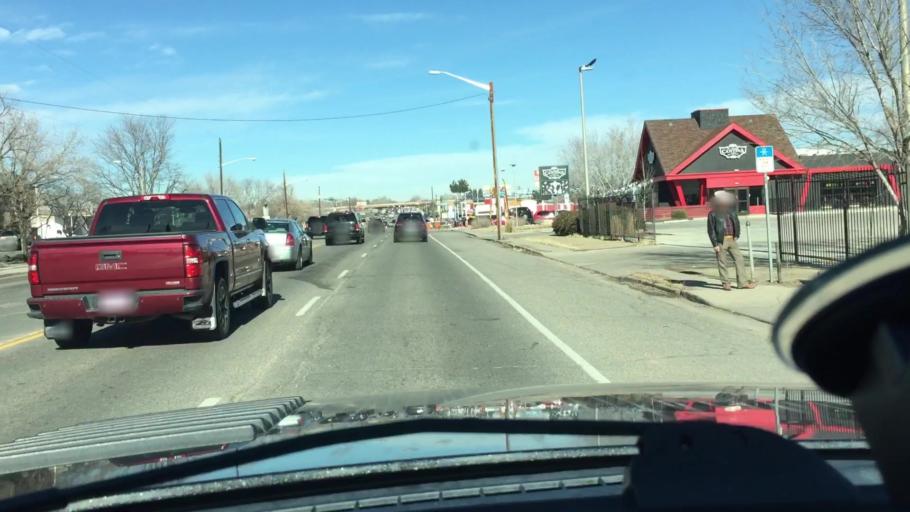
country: US
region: Colorado
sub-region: Adams County
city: Twin Lakes
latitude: 39.8240
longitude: -105.0061
